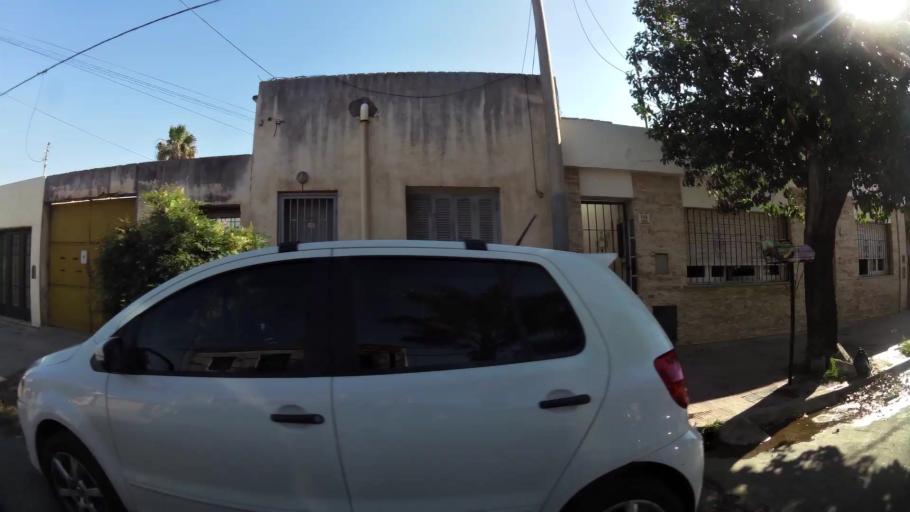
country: AR
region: Cordoba
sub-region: Departamento de Capital
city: Cordoba
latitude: -31.3919
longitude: -64.1746
